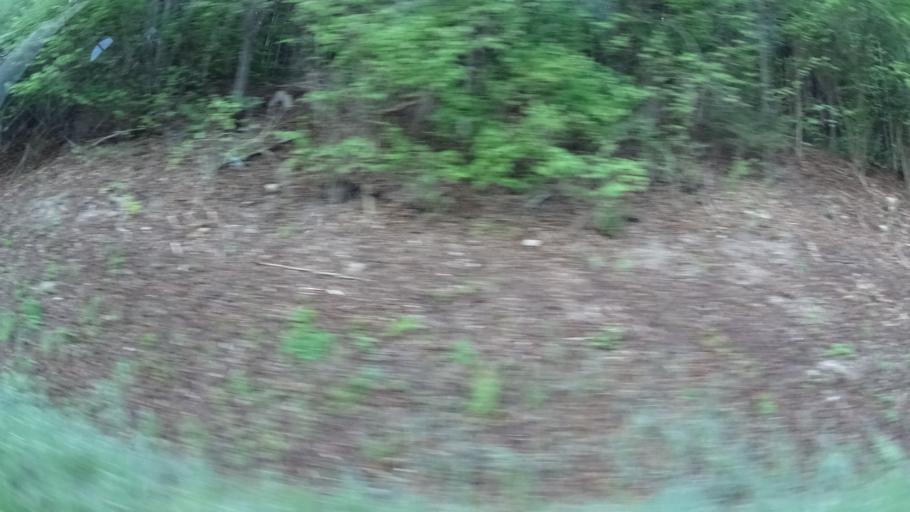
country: DE
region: Baden-Wuerttemberg
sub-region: Tuebingen Region
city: Haigerloch
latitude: 48.4117
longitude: 8.7693
